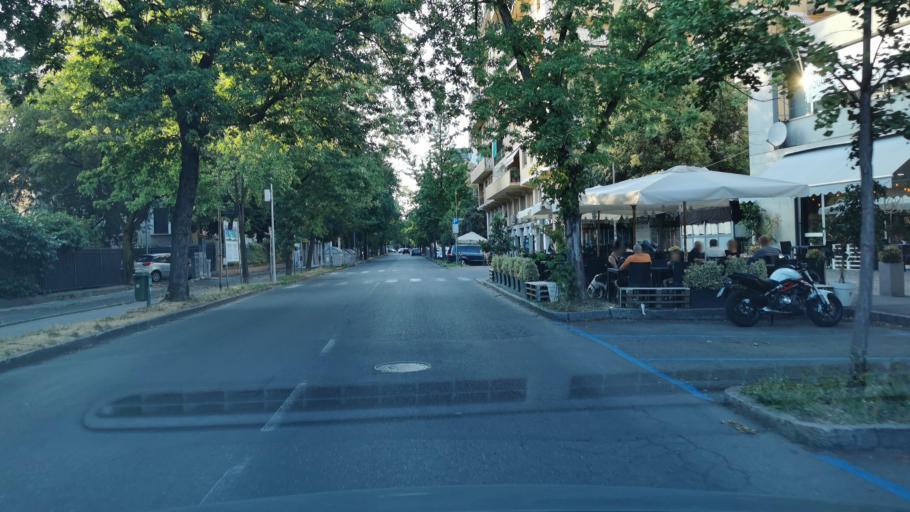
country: IT
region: Emilia-Romagna
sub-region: Provincia di Modena
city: Modena
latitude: 44.6359
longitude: 10.9305
